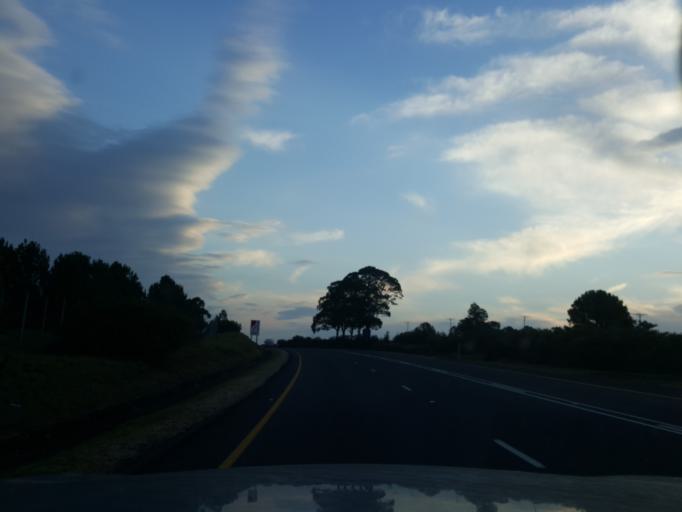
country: ZA
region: Eastern Cape
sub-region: Cacadu District Municipality
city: Grahamstown
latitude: -33.3777
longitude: 26.4517
